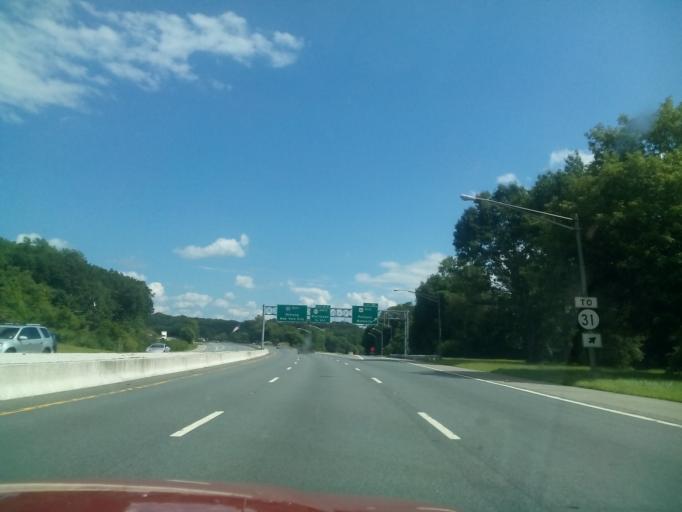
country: US
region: Pennsylvania
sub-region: Northampton County
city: East Bangor
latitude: 40.9301
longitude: -75.0970
